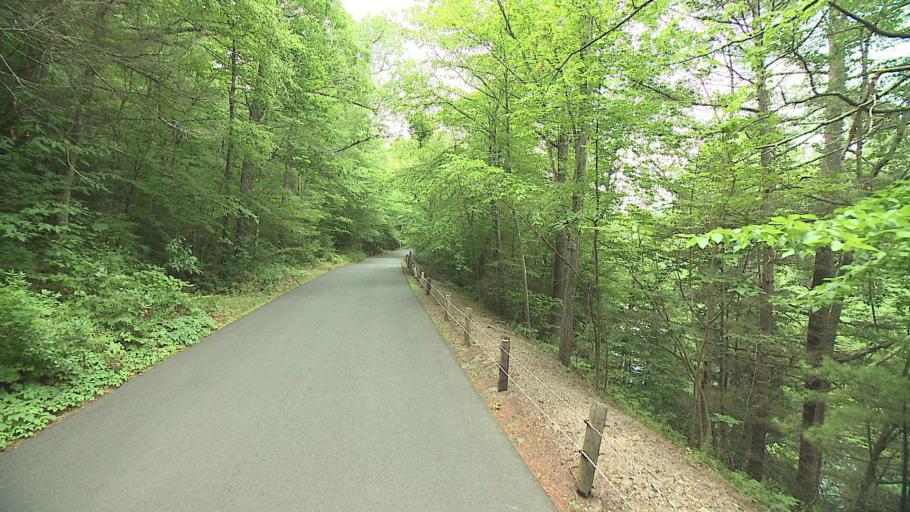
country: US
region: Connecticut
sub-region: Litchfield County
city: New Hartford Center
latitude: 41.9348
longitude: -73.0000
